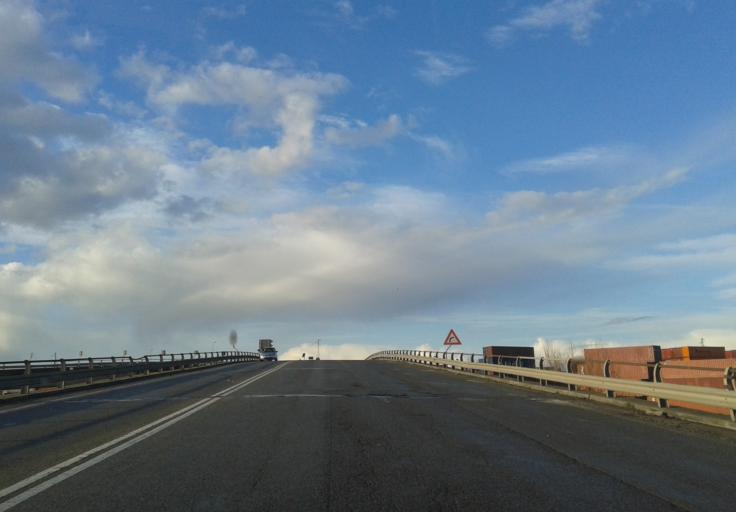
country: IT
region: Tuscany
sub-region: Provincia di Livorno
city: Livorno
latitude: 43.5856
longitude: 10.3245
